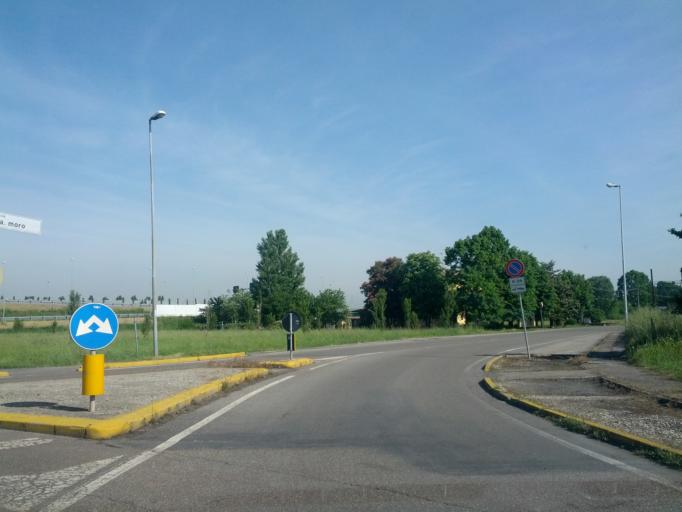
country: IT
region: Emilia-Romagna
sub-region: Provincia di Reggio Emilia
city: Reggio nell'Emilia
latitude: 44.7309
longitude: 10.6414
